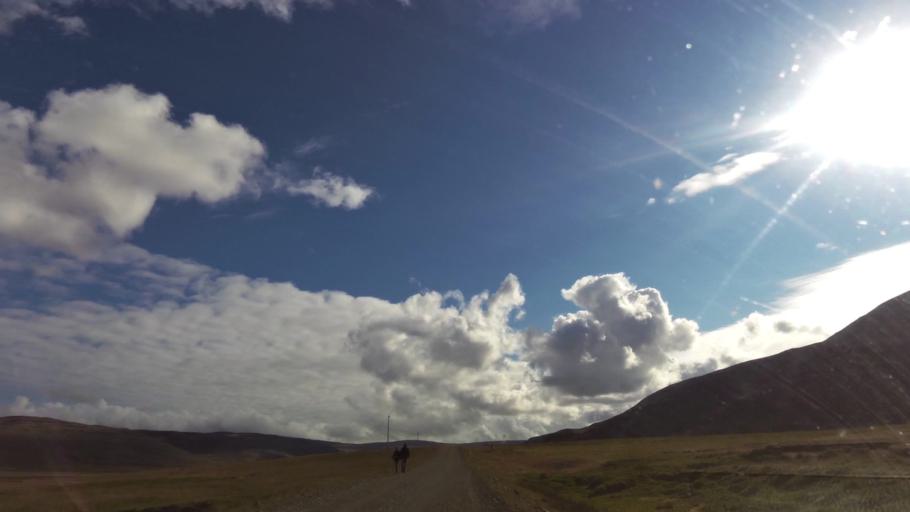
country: IS
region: West
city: Olafsvik
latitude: 65.5889
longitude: -24.1266
